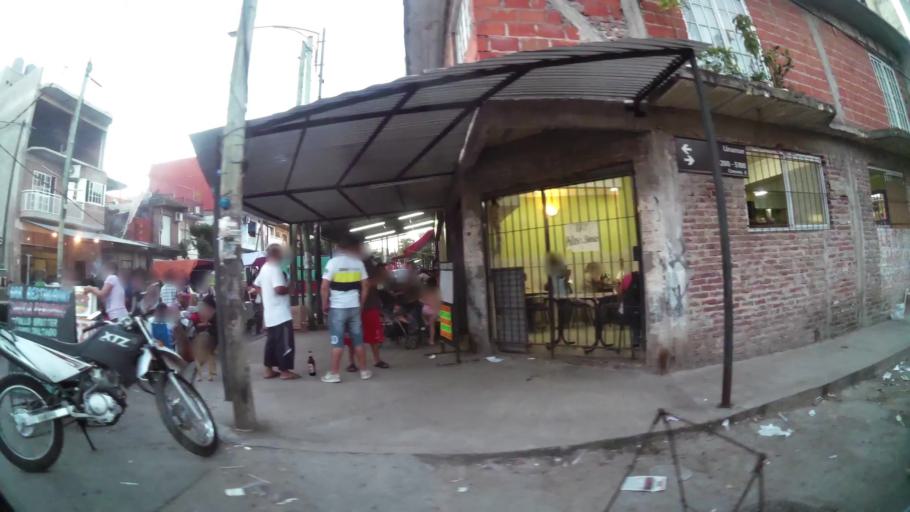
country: AR
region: Buenos Aires F.D.
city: Villa Lugano
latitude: -34.6752
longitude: -58.4681
